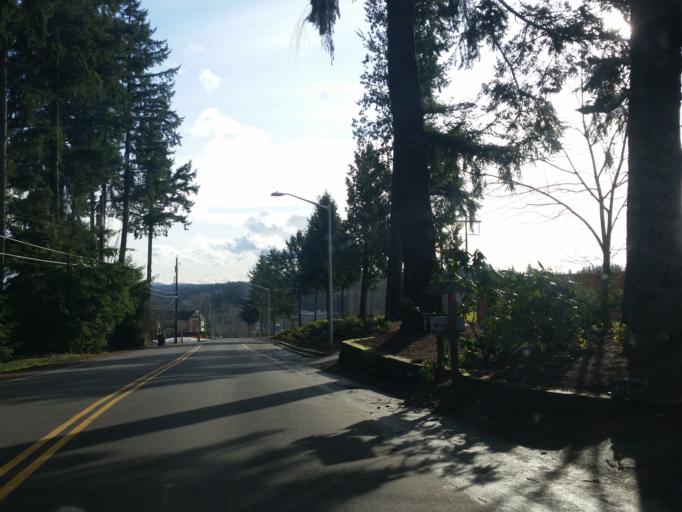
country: US
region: Washington
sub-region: King County
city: Kingsgate
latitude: 47.7180
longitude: -122.1589
